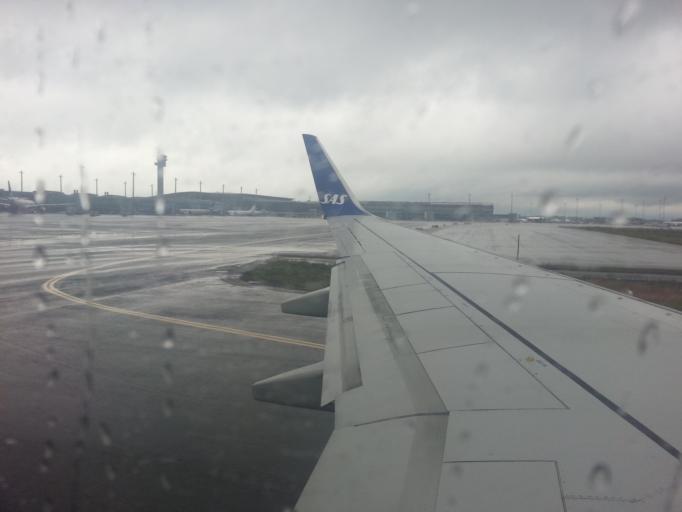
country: NO
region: Akershus
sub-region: Ullensaker
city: Jessheim
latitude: 60.1953
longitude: 11.1135
